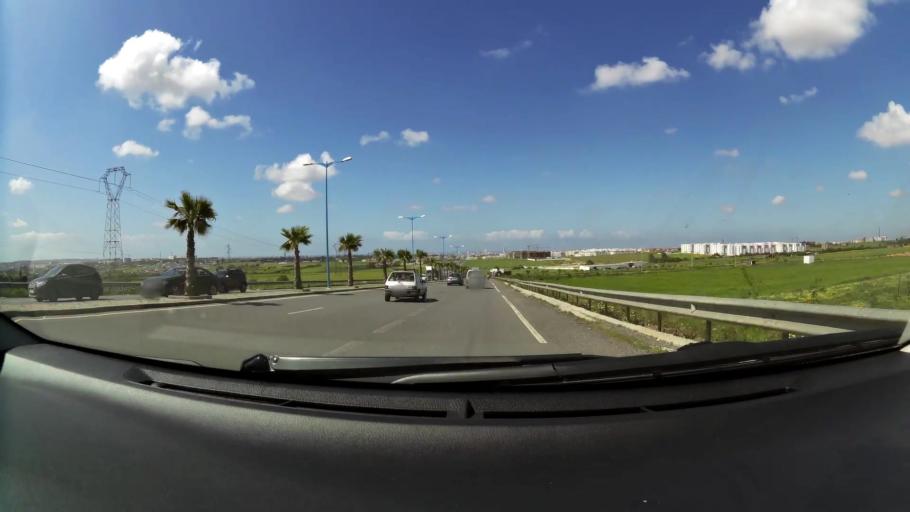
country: MA
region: Grand Casablanca
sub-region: Nouaceur
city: Bouskoura
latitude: 33.5118
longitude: -7.6125
